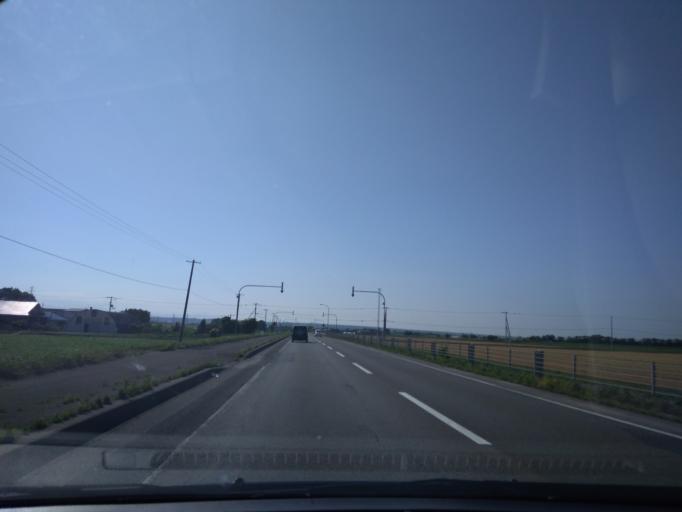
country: JP
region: Hokkaido
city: Kitahiroshima
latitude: 42.9911
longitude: 141.6049
